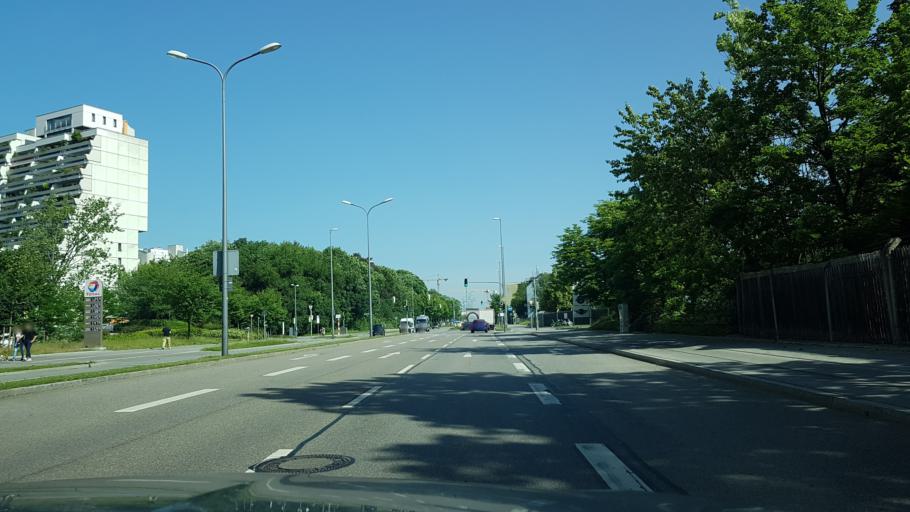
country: DE
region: Bavaria
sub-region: Upper Bavaria
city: Munich
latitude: 48.1820
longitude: 11.5547
